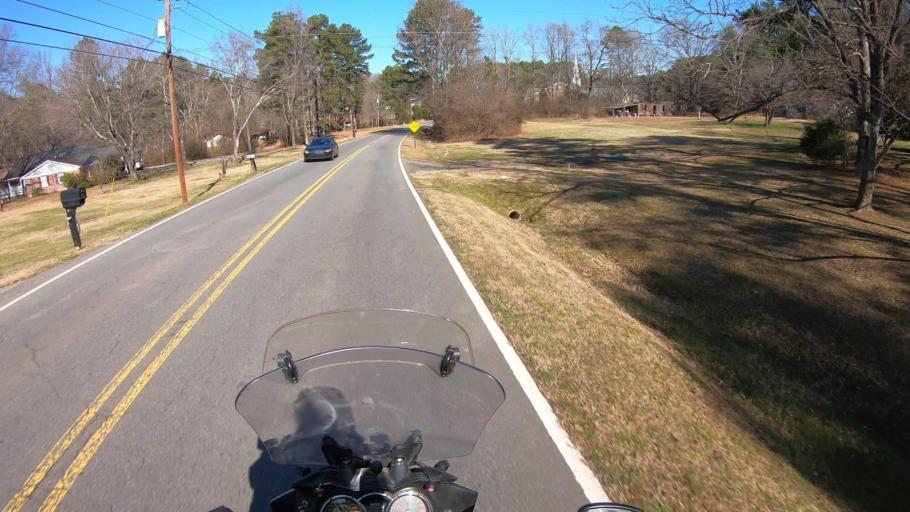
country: US
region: Georgia
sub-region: Bartow County
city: Cartersville
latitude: 34.2572
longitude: -84.8088
